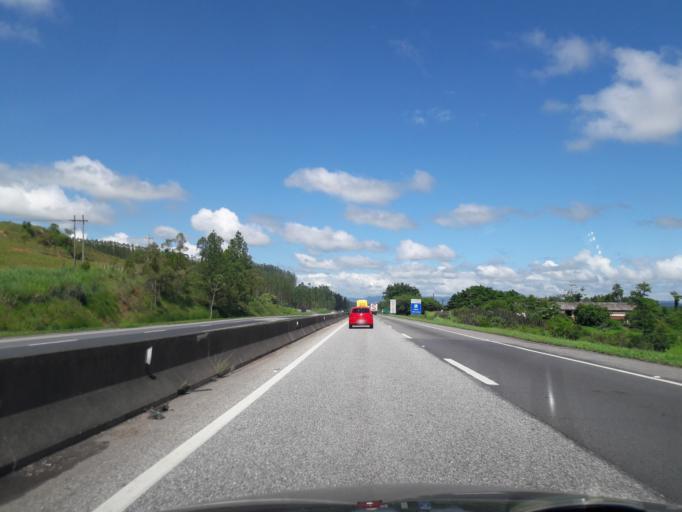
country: BR
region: Sao Paulo
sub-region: Jacupiranga
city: Jacupiranga
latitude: -24.7113
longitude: -48.0230
